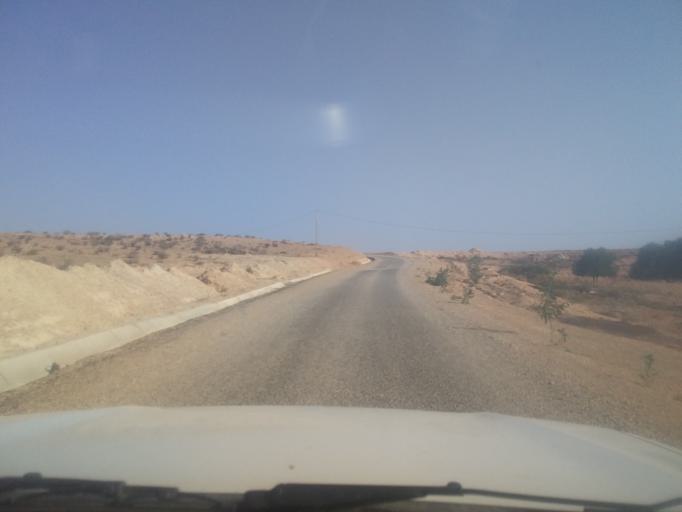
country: TN
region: Qabis
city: Matmata
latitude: 33.5837
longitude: 10.2597
